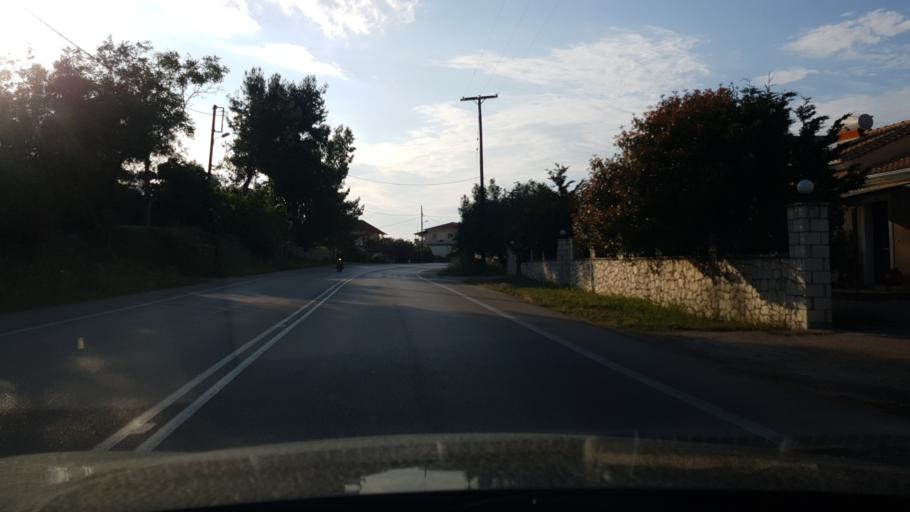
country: GR
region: Ionian Islands
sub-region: Lefkada
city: Lefkada
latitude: 38.8159
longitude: 20.7044
